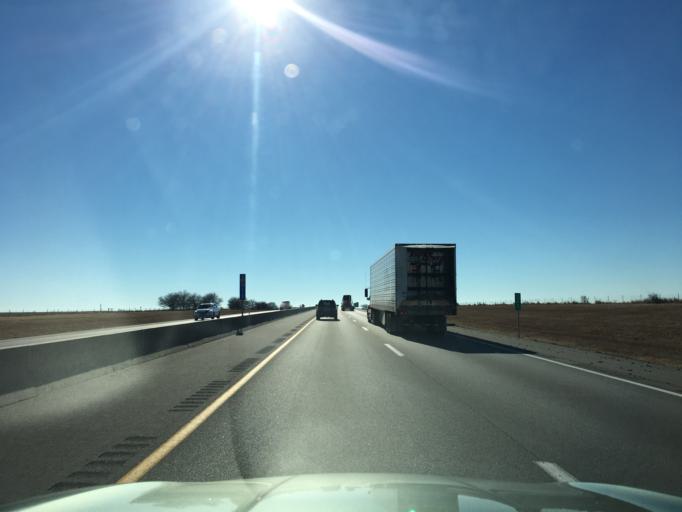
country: US
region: Kansas
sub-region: Sumner County
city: Wellington
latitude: 37.3030
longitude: -97.3405
